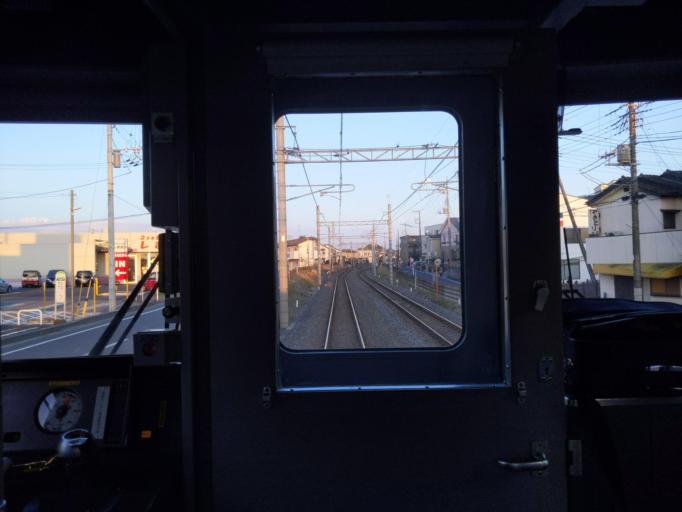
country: JP
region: Chiba
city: Noda
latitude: 35.9811
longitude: 139.8131
